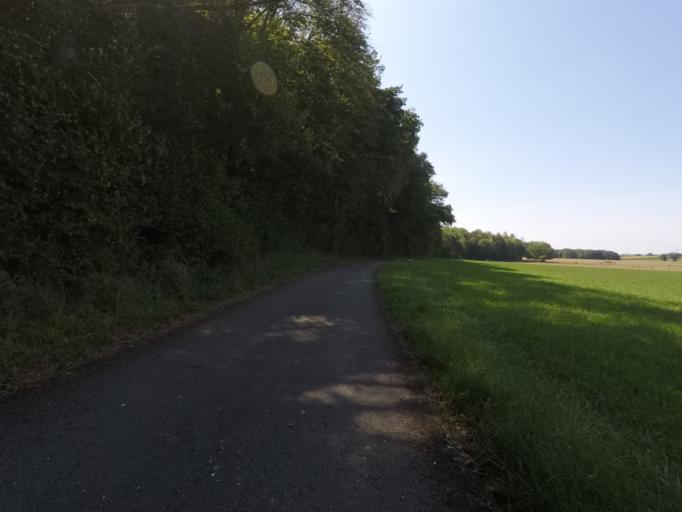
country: LU
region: Luxembourg
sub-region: Canton de Capellen
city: Garnich
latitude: 49.6335
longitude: 5.9405
